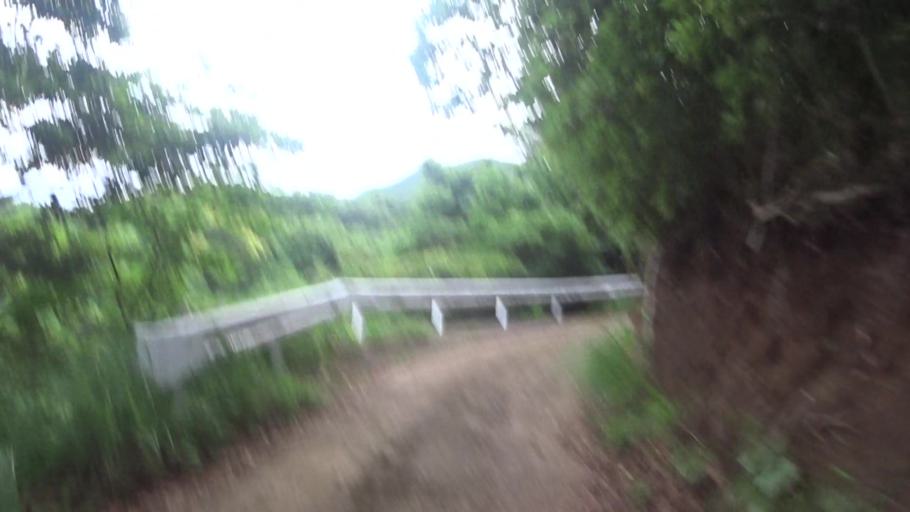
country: JP
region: Nagasaki
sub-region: Hirado Shi
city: Hirado
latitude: 33.1826
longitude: 129.3536
